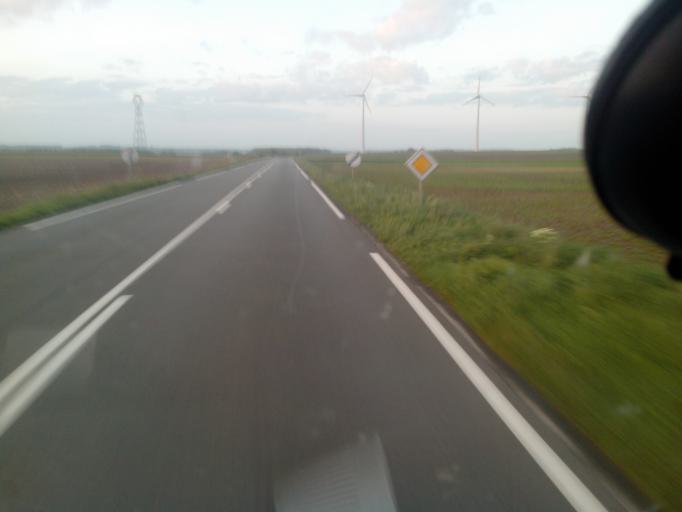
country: FR
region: Picardie
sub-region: Departement de la Somme
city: Crecy-en-Ponthieu
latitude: 50.2438
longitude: 1.9550
